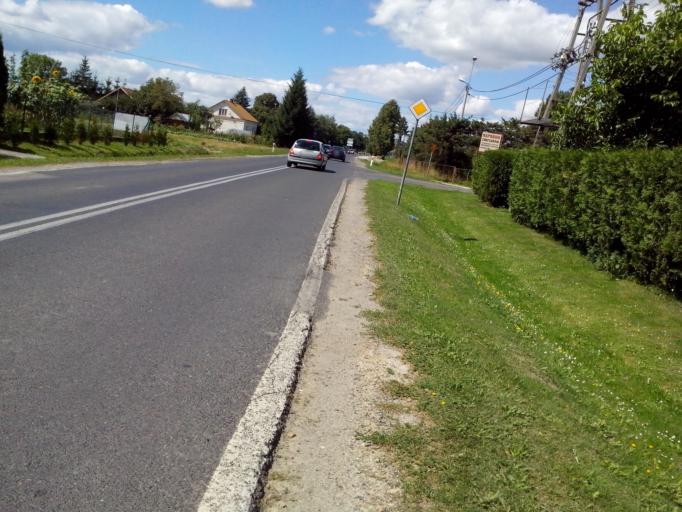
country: PL
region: Subcarpathian Voivodeship
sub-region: Powiat strzyzowski
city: Strzyzow
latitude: 49.8401
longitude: 21.8204
